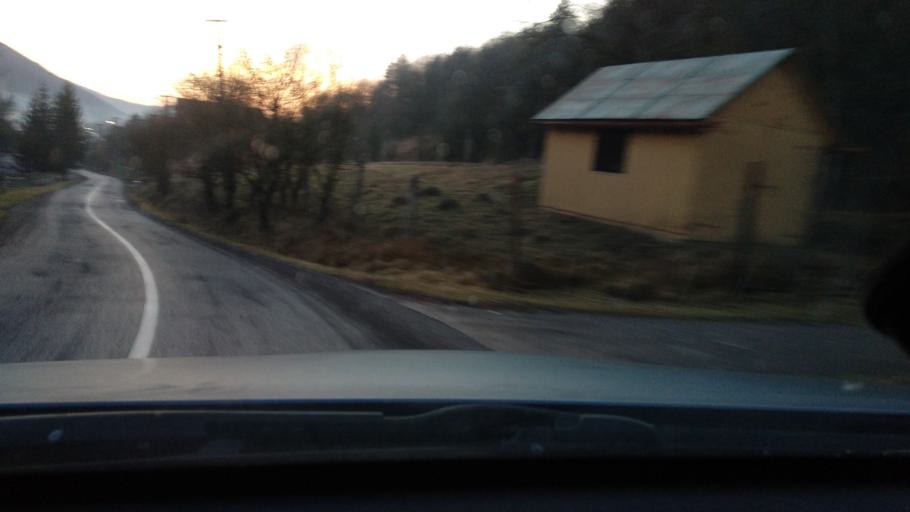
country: SK
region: Nitriansky
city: Banovce nad Bebravou
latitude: 48.8567
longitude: 18.3000
